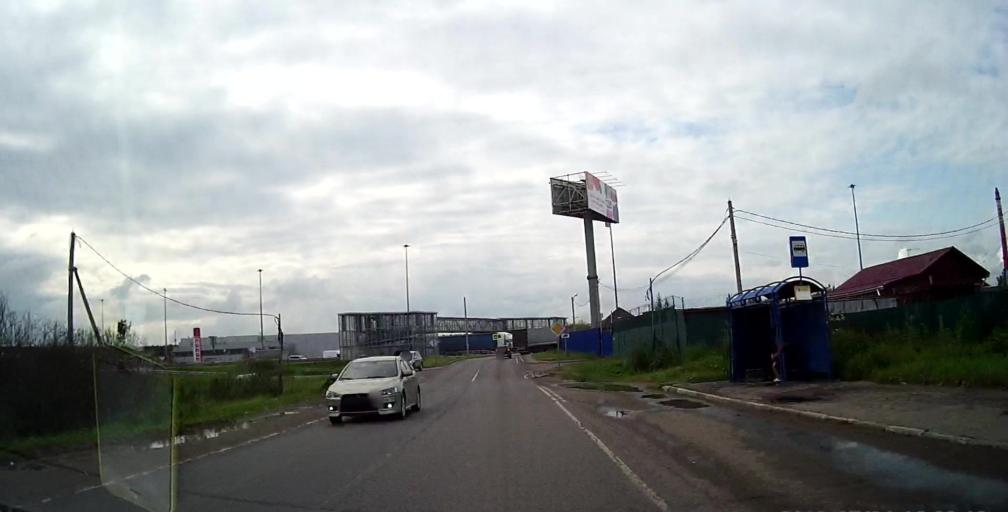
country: RU
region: Moskovskaya
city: Klimovsk
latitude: 55.3886
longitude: 37.5540
